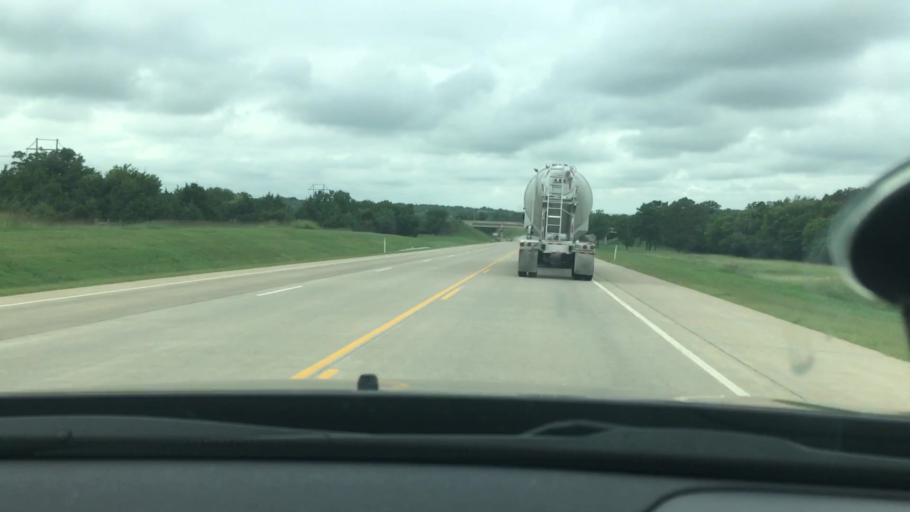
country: US
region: Oklahoma
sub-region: Murray County
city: Sulphur
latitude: 34.5960
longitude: -96.8929
